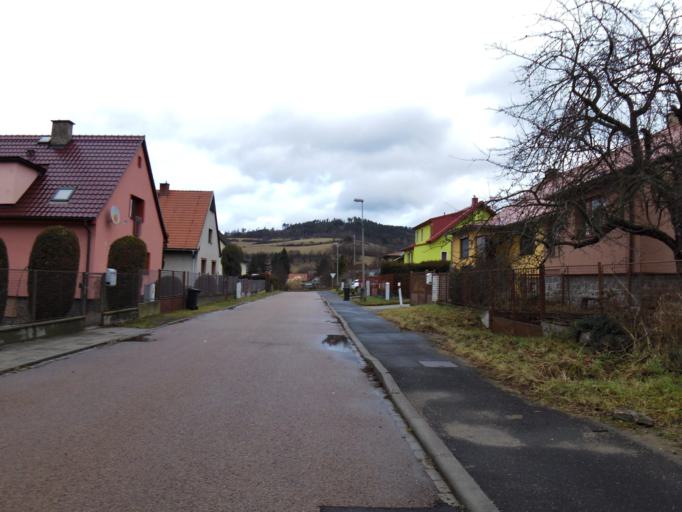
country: CZ
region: Plzensky
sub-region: Okres Klatovy
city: Susice
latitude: 49.2265
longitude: 13.5220
